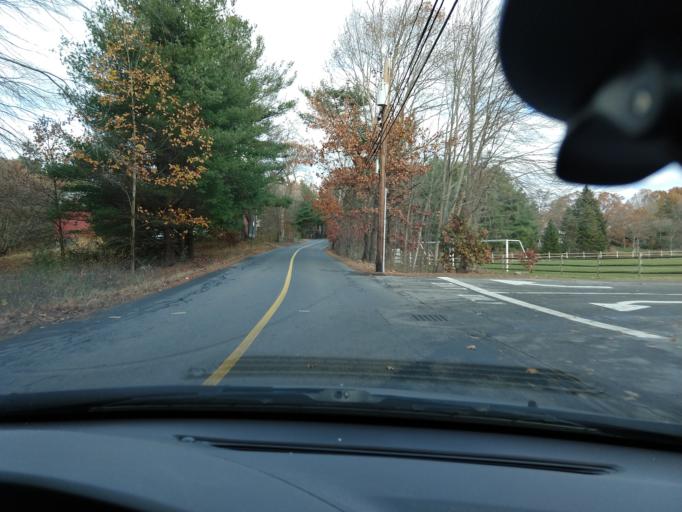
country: US
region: Massachusetts
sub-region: Middlesex County
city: West Concord
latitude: 42.4792
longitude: -71.3814
